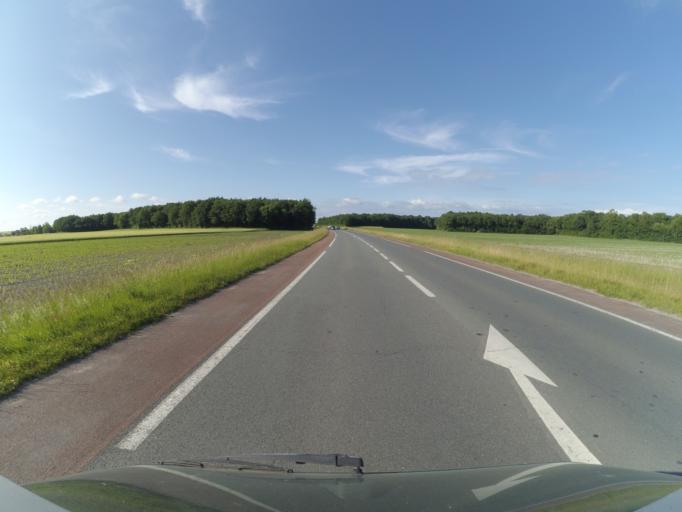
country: FR
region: Poitou-Charentes
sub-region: Departement de la Charente-Maritime
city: Saint-Sulpice-de-Royan
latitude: 45.6748
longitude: -0.9988
